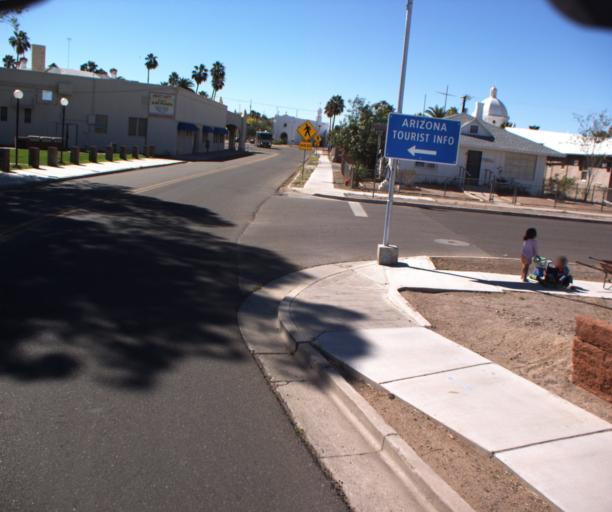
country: US
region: Arizona
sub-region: Pima County
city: Ajo
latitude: 32.3743
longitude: -112.8631
